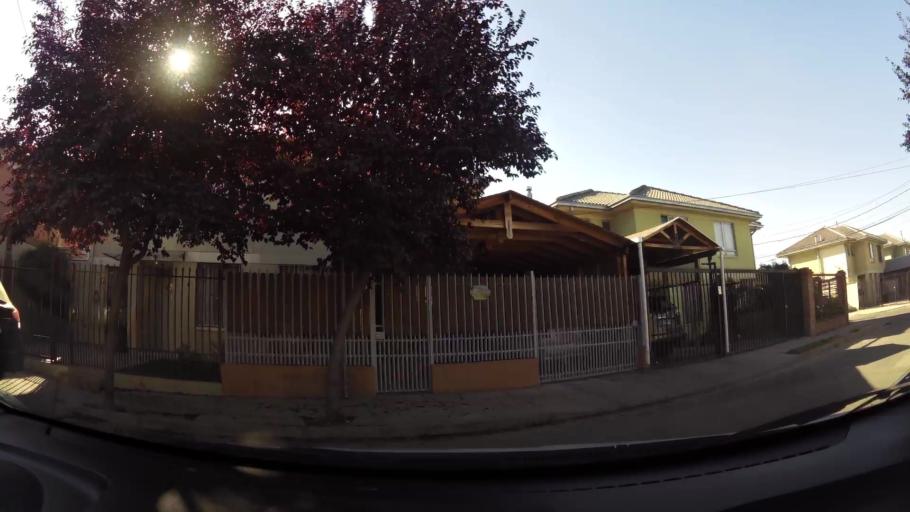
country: CL
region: O'Higgins
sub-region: Provincia de Cachapoal
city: Rancagua
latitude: -34.1816
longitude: -70.7603
